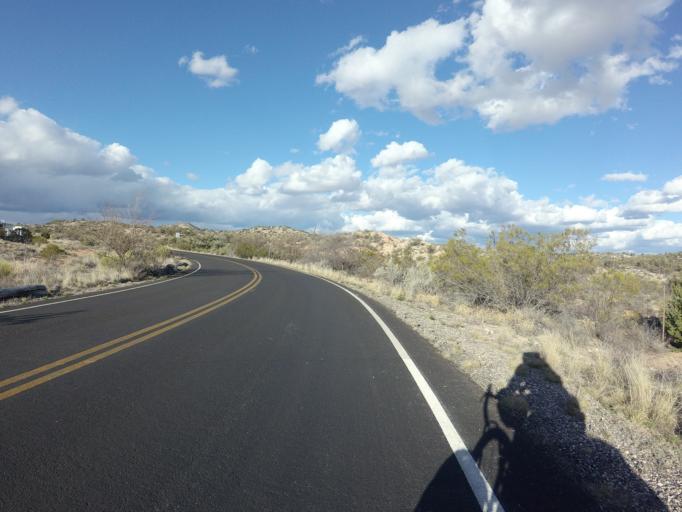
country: US
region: Arizona
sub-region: Yavapai County
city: Cottonwood
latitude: 34.7587
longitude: -112.0146
